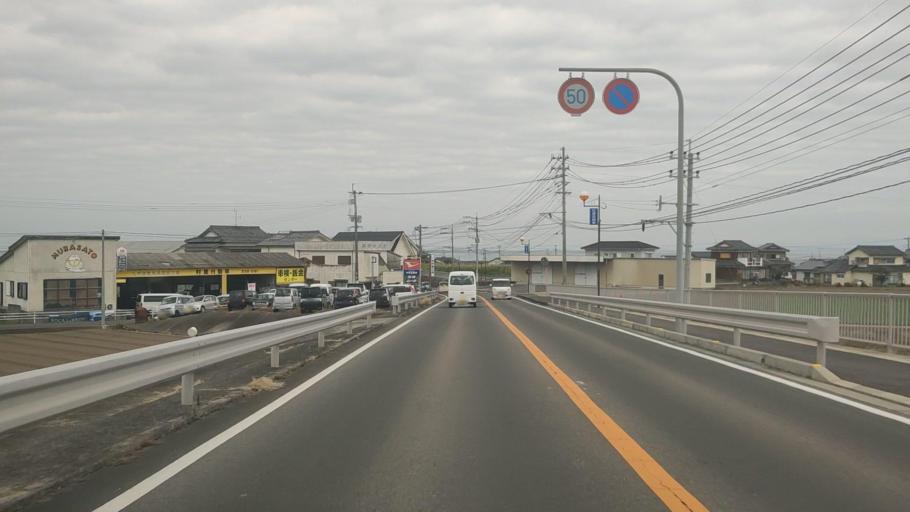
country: JP
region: Nagasaki
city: Shimabara
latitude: 32.8525
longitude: 130.3378
